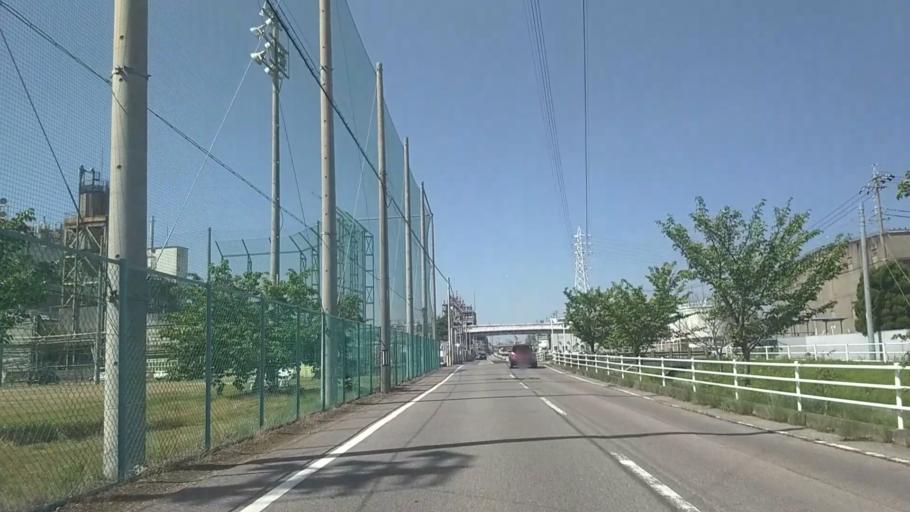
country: JP
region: Aichi
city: Okazaki
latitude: 34.9740
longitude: 137.1566
